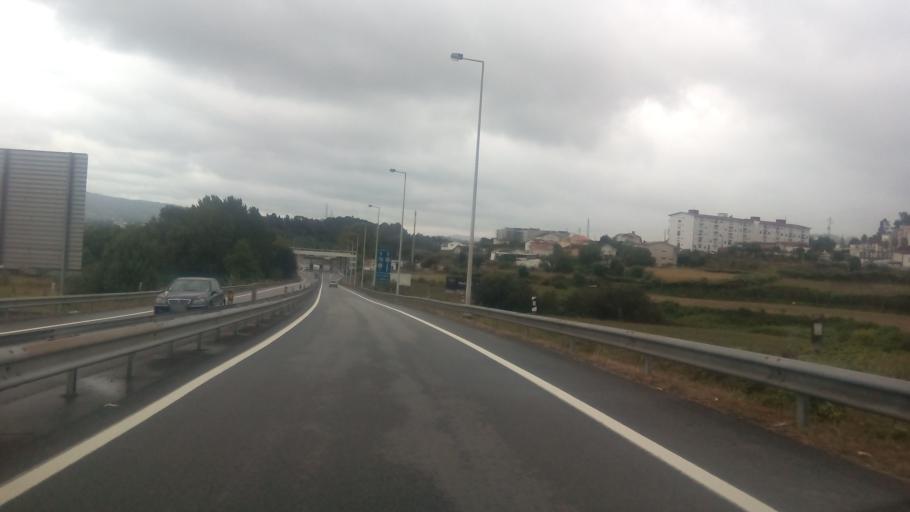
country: PT
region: Porto
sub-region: Paredes
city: Casteloes de Cepeda
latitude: 41.2050
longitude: -8.3364
